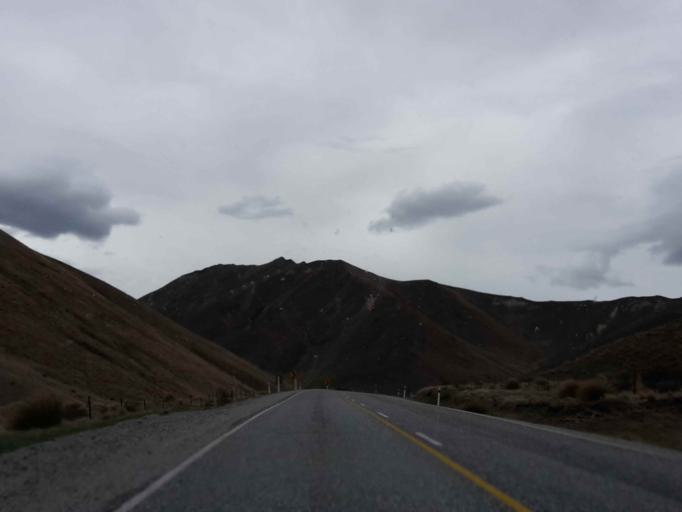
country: NZ
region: Otago
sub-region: Queenstown-Lakes District
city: Wanaka
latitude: -44.5787
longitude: 169.6145
